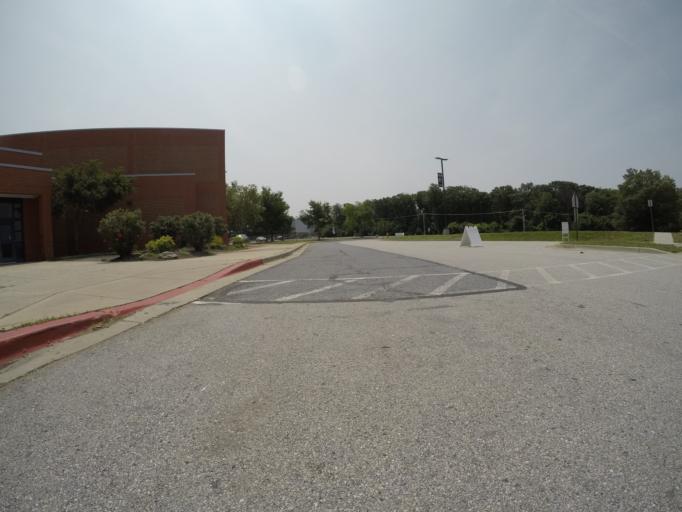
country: US
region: Maryland
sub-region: Howard County
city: Columbia
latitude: 39.2256
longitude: -76.8125
